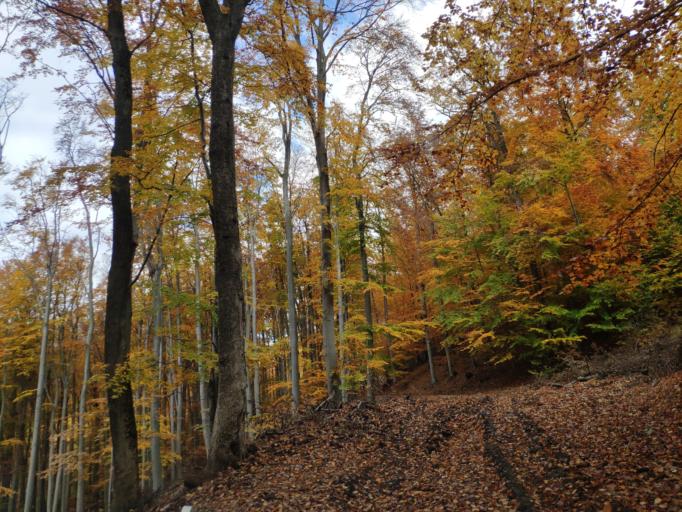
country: SK
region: Kosicky
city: Medzev
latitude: 48.7345
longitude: 20.9873
